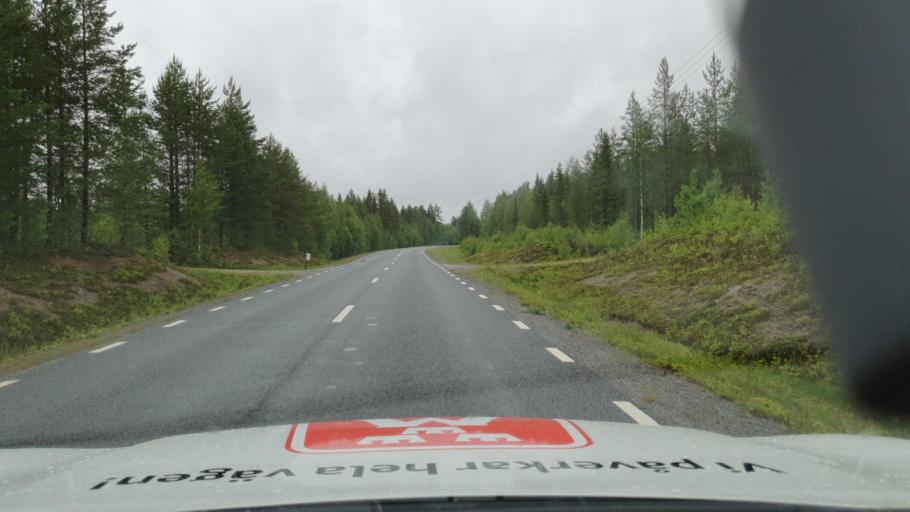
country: SE
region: Vaesterbotten
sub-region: Asele Kommun
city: Asele
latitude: 63.9300
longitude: 17.2653
